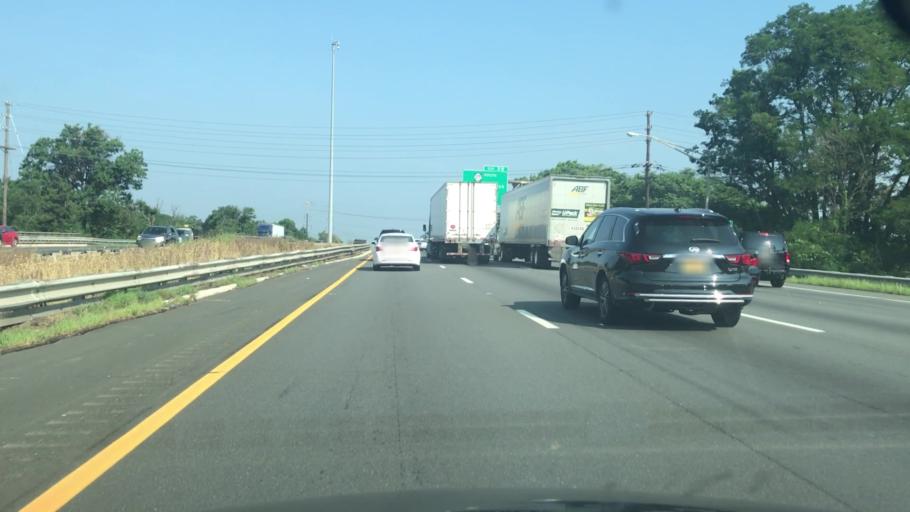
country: US
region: New Jersey
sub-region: Middlesex County
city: Metuchen
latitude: 40.5333
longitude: -74.3762
